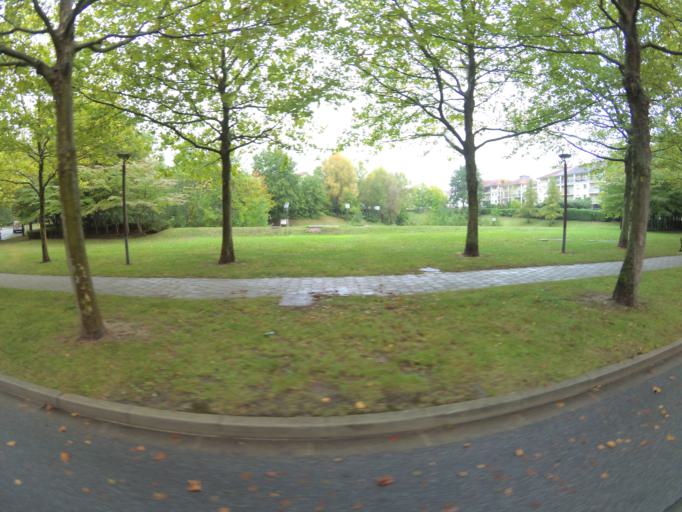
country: FR
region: Ile-de-France
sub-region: Departement de Seine-et-Marne
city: Bussy-Saint-Georges
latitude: 48.8375
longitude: 2.7066
